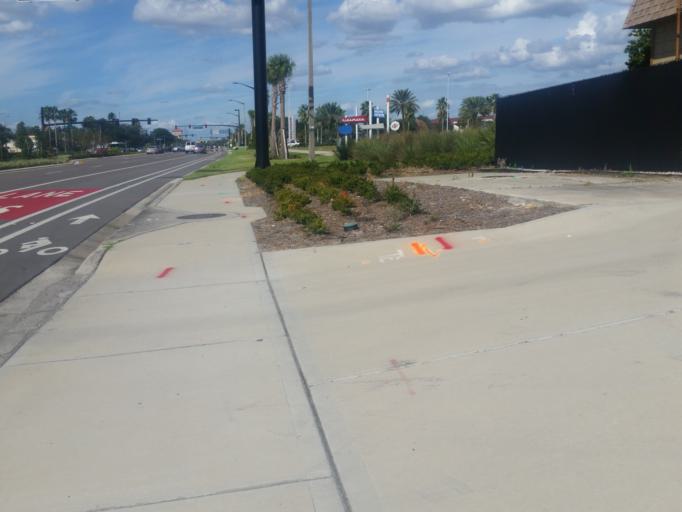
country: US
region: Florida
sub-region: Orange County
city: Tangelo Park
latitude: 28.4652
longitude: -81.4502
